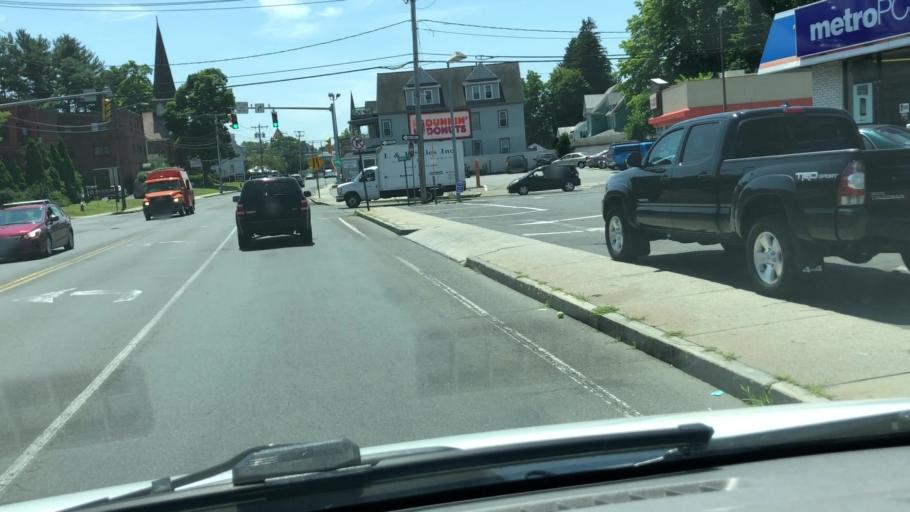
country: US
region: Massachusetts
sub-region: Hampshire County
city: Northampton
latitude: 42.3244
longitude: -72.6330
